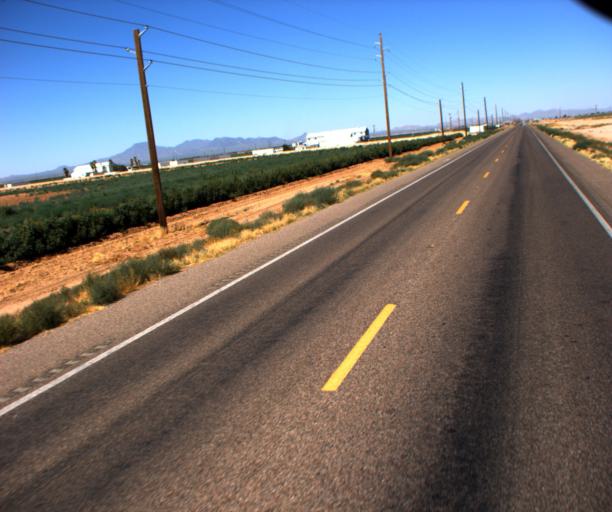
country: US
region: Arizona
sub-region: Pinal County
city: Casa Grande
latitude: 32.8794
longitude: -111.9068
